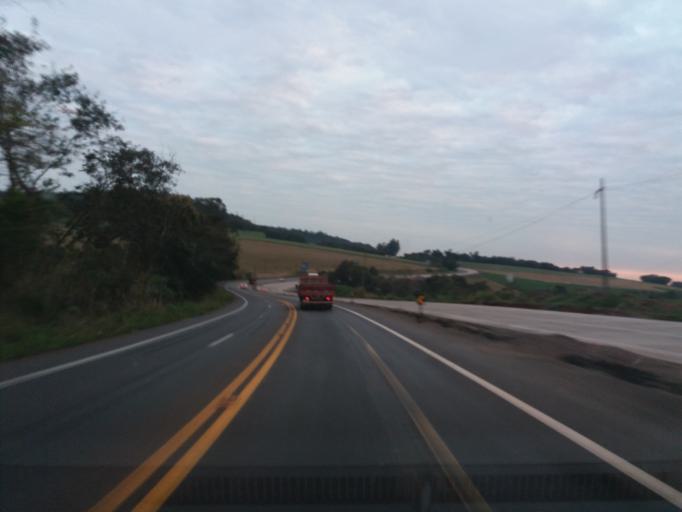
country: BR
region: Parana
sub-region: Realeza
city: Realeza
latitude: -25.3825
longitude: -53.5771
